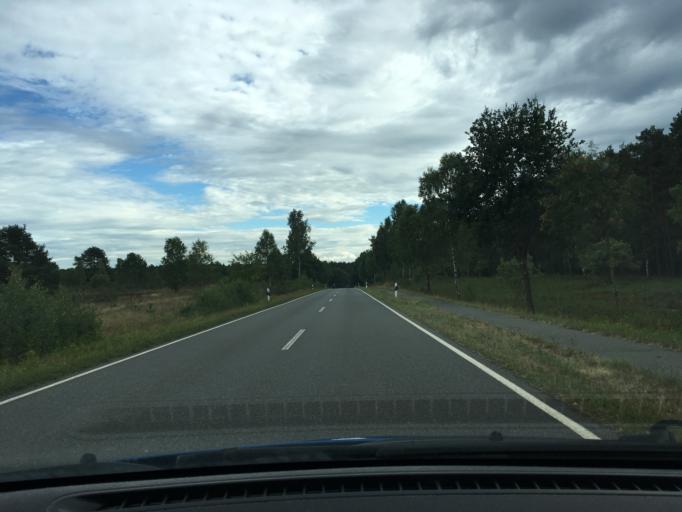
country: DE
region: Lower Saxony
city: Undeloh
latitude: 53.2408
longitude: 9.9190
